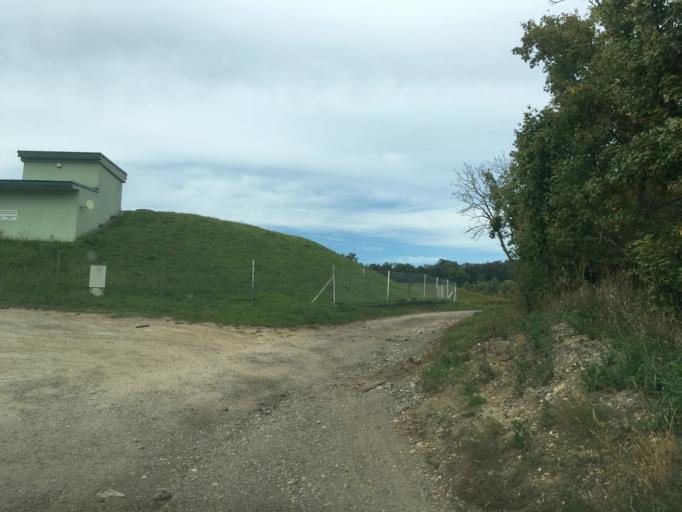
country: AT
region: Burgenland
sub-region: Eisenstadt-Umgebung
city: Breitenbrunn
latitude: 47.9598
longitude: 16.7338
